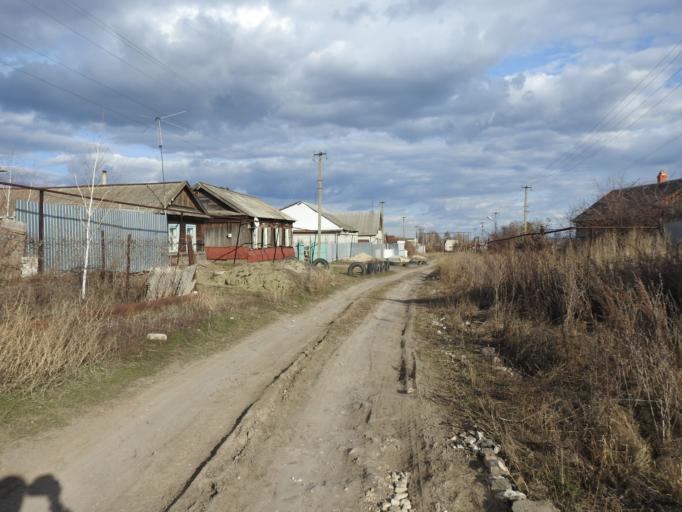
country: RU
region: Saratov
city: Sokolovyy
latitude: 51.3816
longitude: 45.8461
